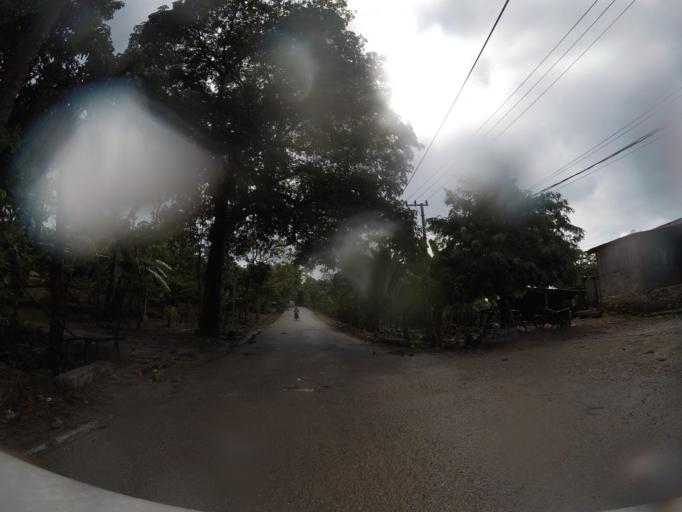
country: TL
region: Baucau
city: Baucau
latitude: -8.4814
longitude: 126.4578
